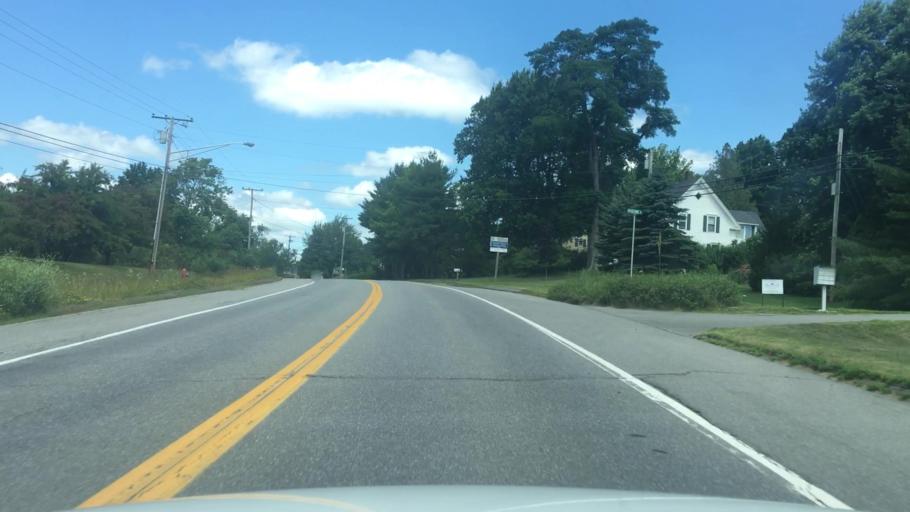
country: US
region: Maine
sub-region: Waldo County
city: Belfast
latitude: 44.3985
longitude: -68.9872
